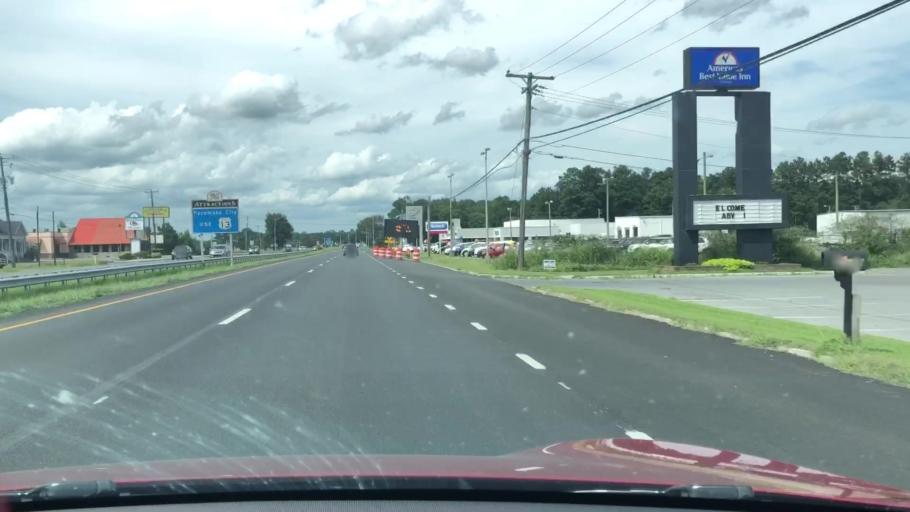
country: US
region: Maryland
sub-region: Worcester County
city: Pocomoke City
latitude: 38.0520
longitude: -75.5434
